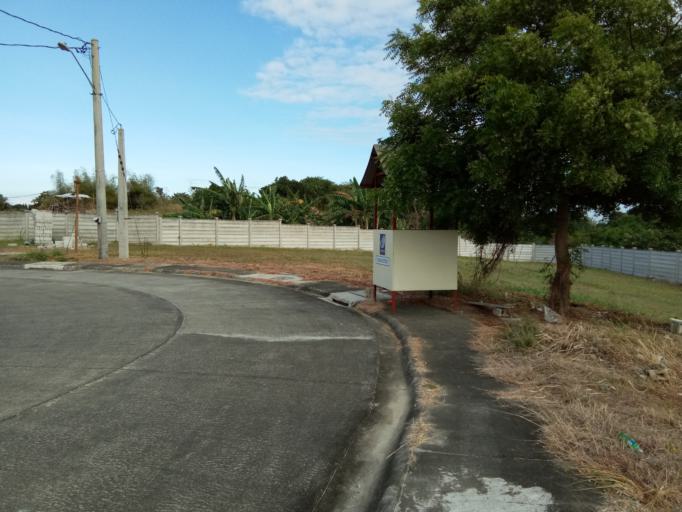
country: PH
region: Calabarzon
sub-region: Province of Cavite
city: Bulihan
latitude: 14.2812
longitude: 120.9732
